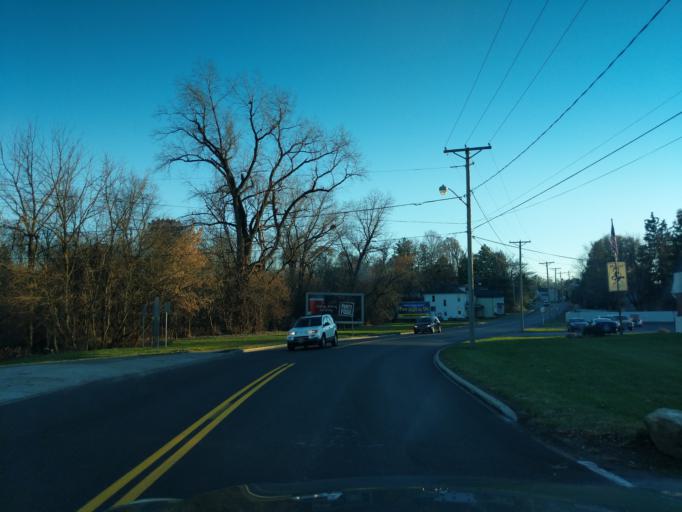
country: US
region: Ohio
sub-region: Licking County
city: Newark
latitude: 40.0464
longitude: -82.4030
